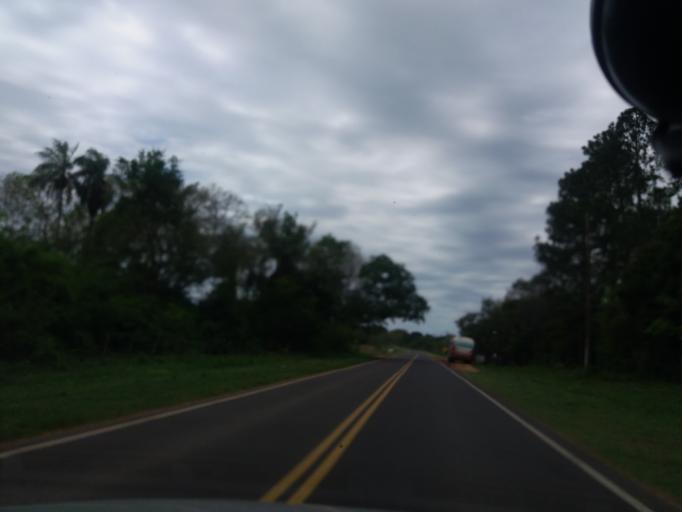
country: AR
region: Corrientes
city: Riachuelo
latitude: -27.4566
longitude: -58.7007
